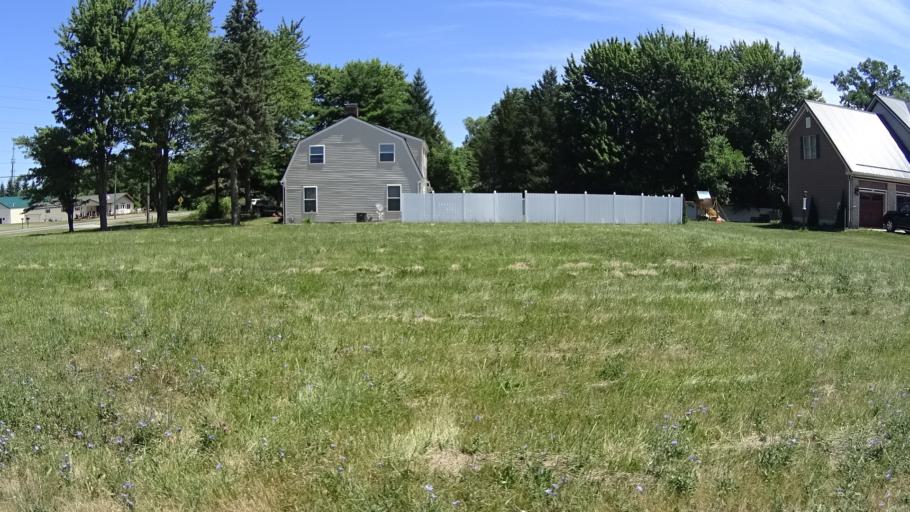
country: US
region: Ohio
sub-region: Erie County
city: Sandusky
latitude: 41.3954
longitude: -82.6572
